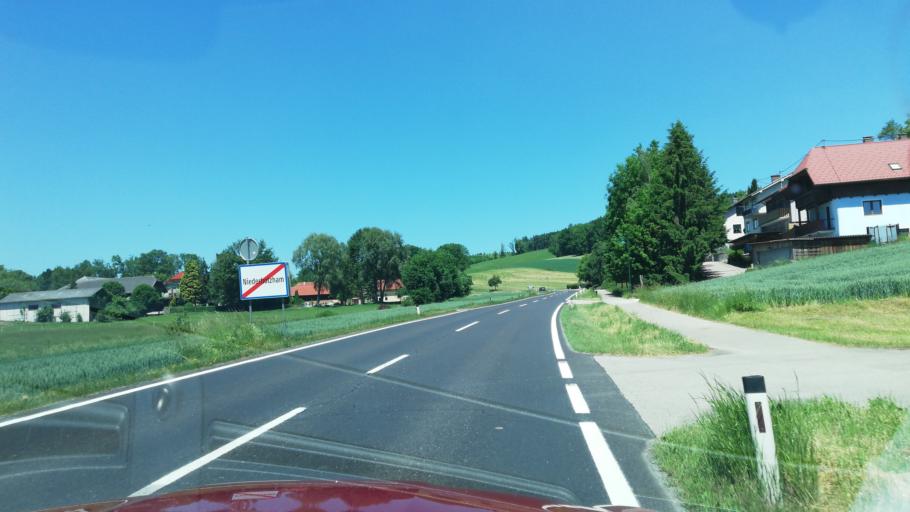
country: AT
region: Upper Austria
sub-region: Politischer Bezirk Vocklabruck
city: Oberndorf bei Schwanenstadt
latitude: 48.0706
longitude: 13.7648
